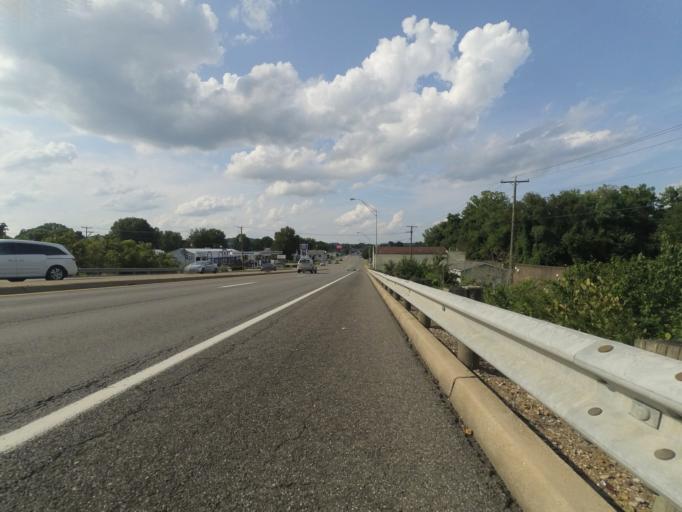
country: US
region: West Virginia
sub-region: Cabell County
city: Huntington
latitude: 38.4237
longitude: -82.3924
